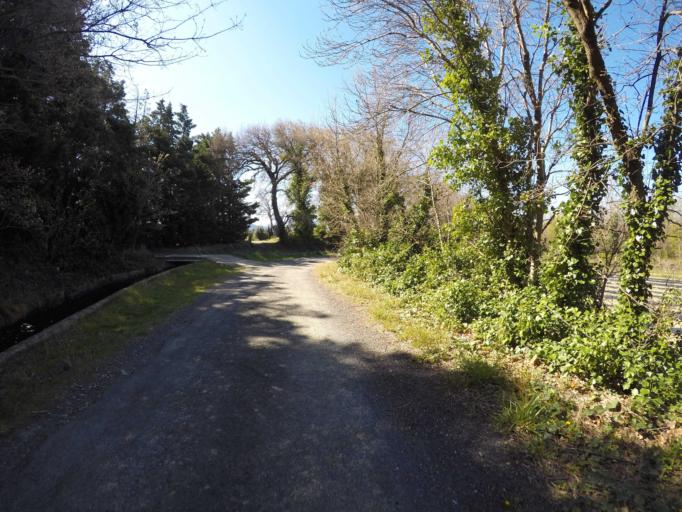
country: FR
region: Languedoc-Roussillon
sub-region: Departement des Pyrenees-Orientales
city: Millas
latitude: 42.6910
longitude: 2.6559
